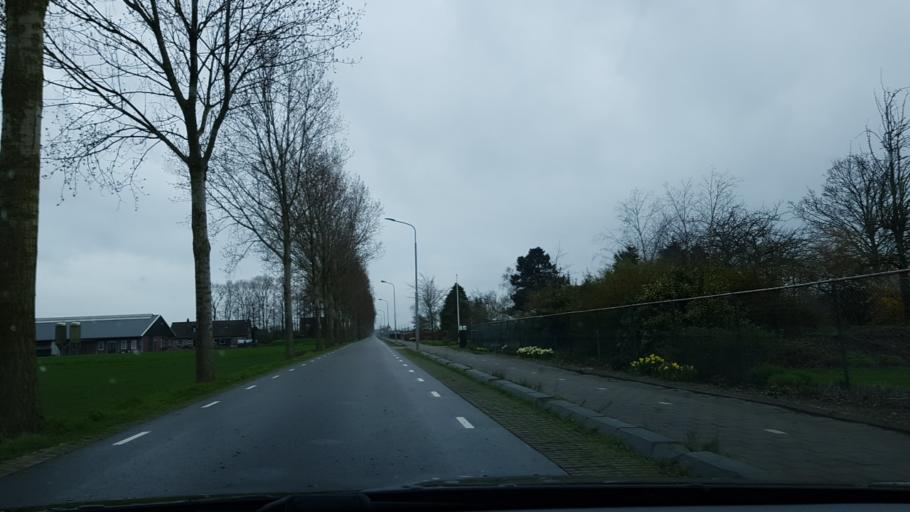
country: NL
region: North Holland
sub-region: Gemeente Haarlemmermeer
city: Hoofddorp
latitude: 52.2656
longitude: 4.6753
